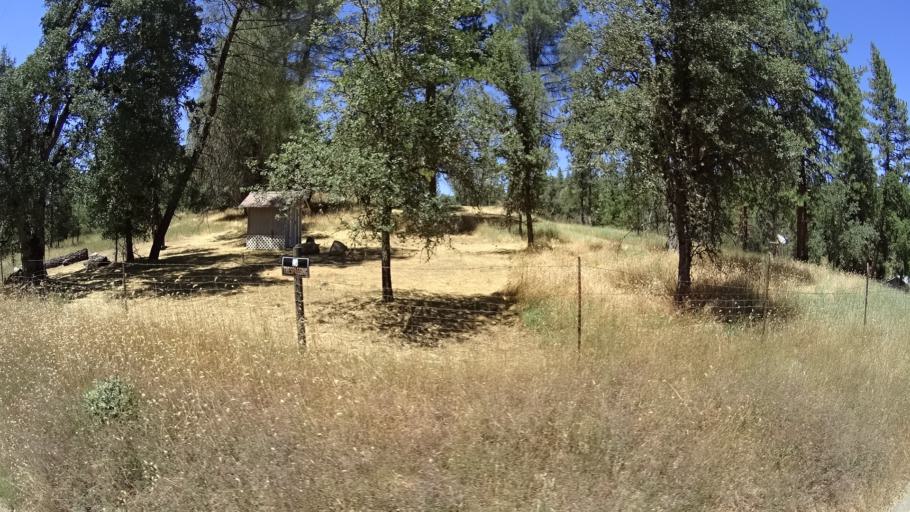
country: US
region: California
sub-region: Calaveras County
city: Mountain Ranch
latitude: 38.2632
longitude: -120.4847
